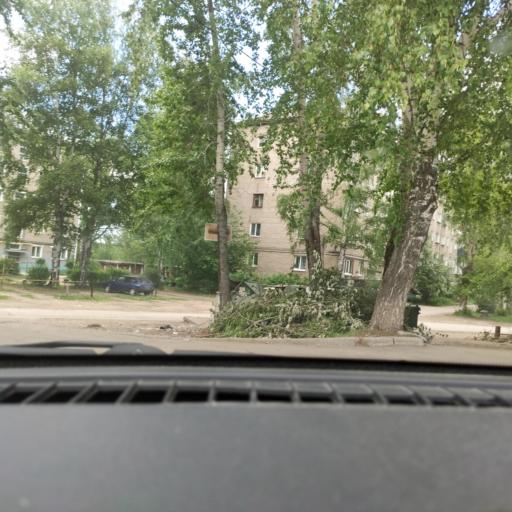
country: RU
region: Perm
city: Krasnokamsk
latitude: 58.0873
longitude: 55.7519
